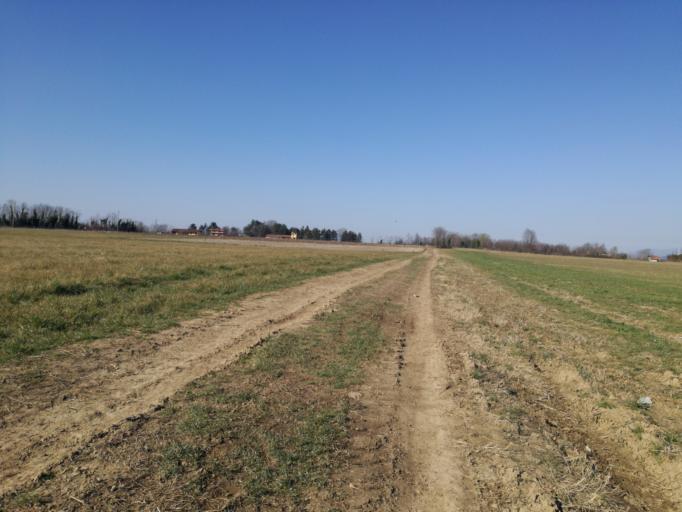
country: IT
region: Lombardy
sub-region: Provincia di Lecco
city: Verderio Inferiore
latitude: 45.6516
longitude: 9.4374
